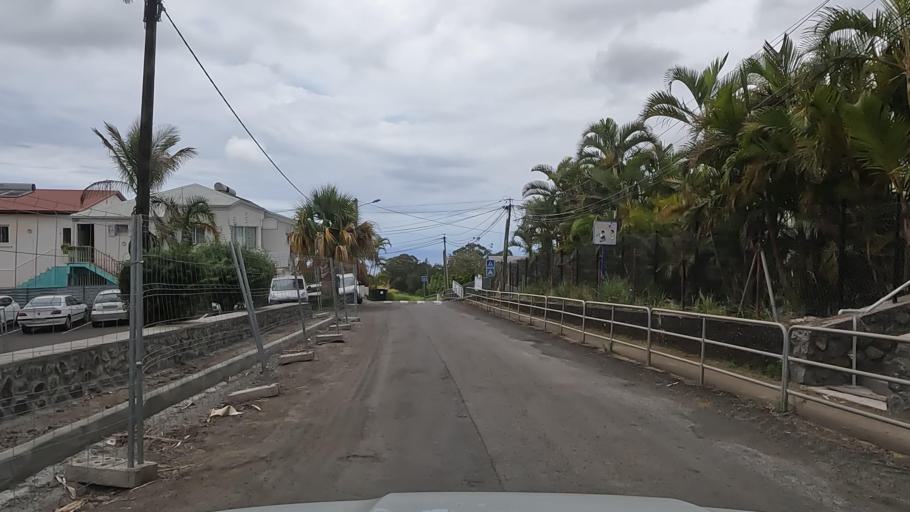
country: RE
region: Reunion
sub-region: Reunion
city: Le Tampon
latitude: -21.3106
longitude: 55.5373
